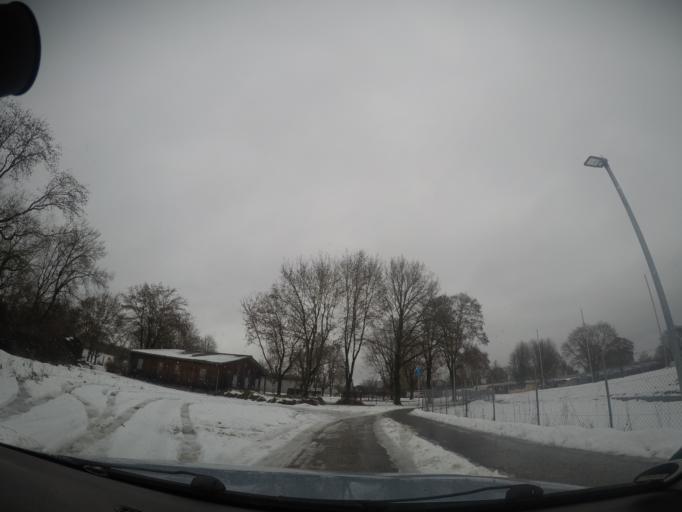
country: DE
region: Bavaria
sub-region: Swabia
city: Neu-Ulm
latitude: 48.3789
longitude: 9.9986
